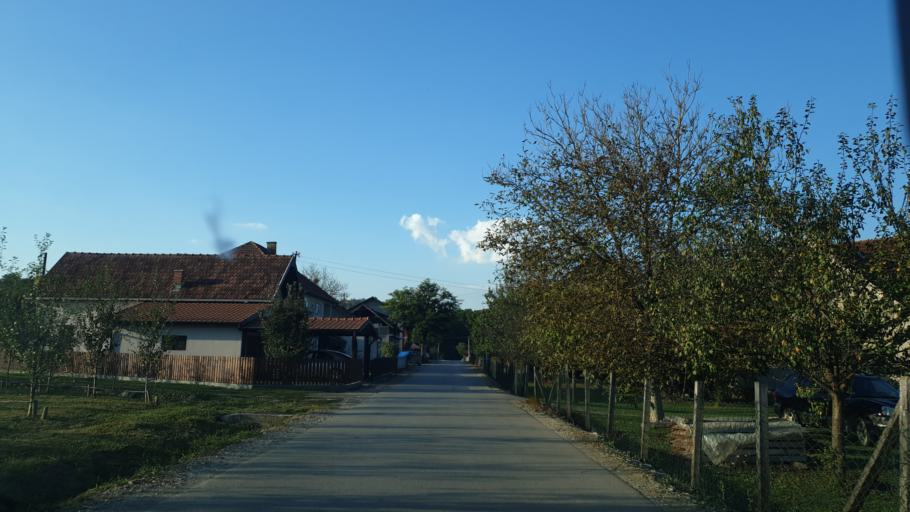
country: RS
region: Central Serbia
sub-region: Zlatiborski Okrug
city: Pozega
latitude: 43.8695
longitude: 19.9914
